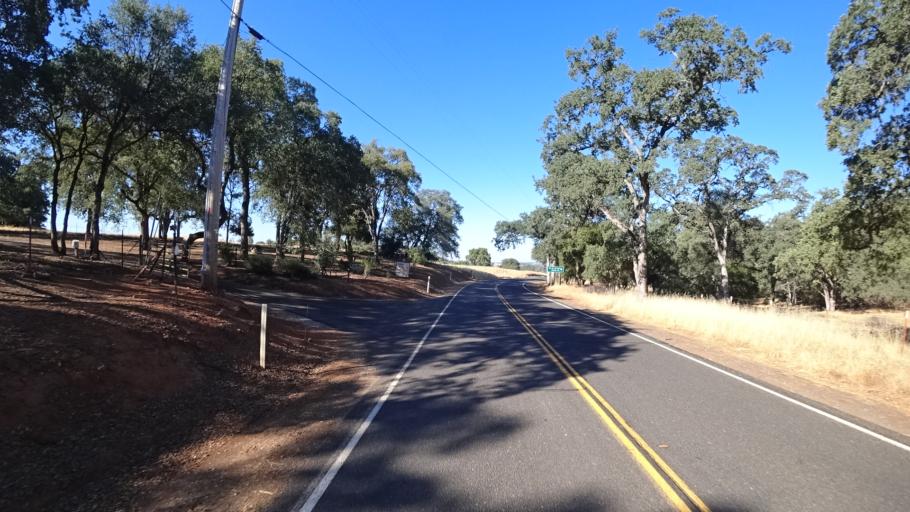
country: US
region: California
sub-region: Calaveras County
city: Angels Camp
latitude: 38.0775
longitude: -120.4879
